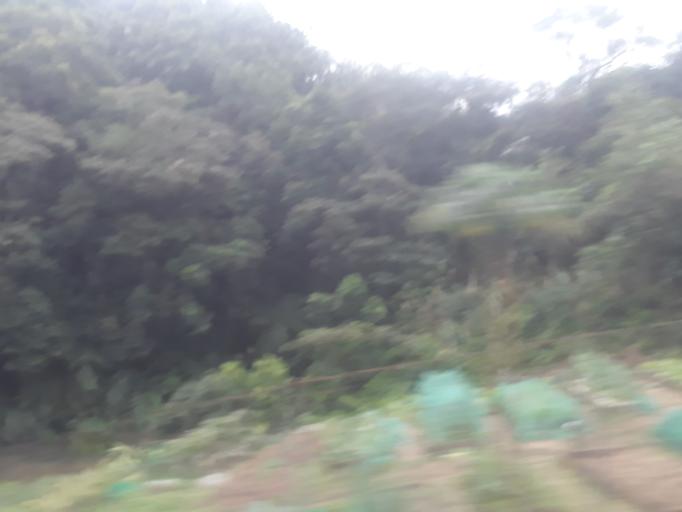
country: TW
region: Taipei
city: Taipei
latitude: 24.9985
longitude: 121.5669
